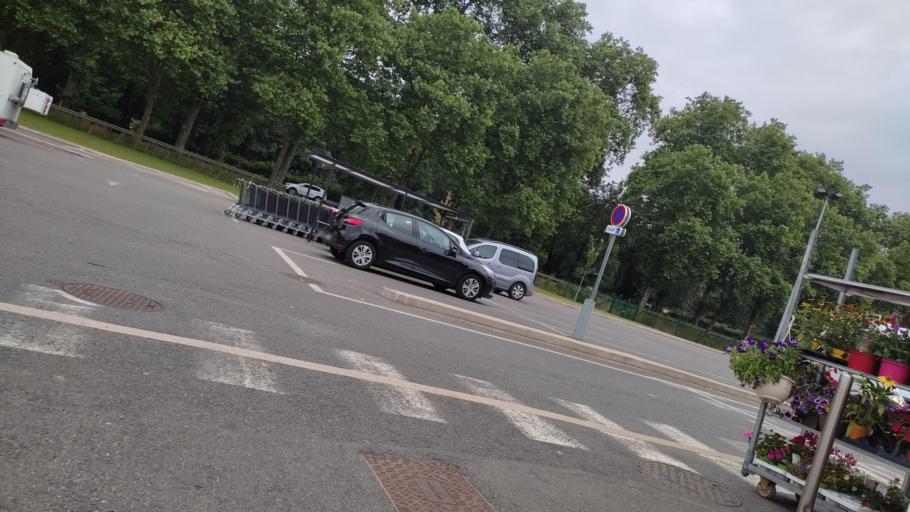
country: FR
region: Bourgogne
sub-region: Departement de la Nievre
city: Chatillon-en-Bazois
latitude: 47.0455
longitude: 3.6444
